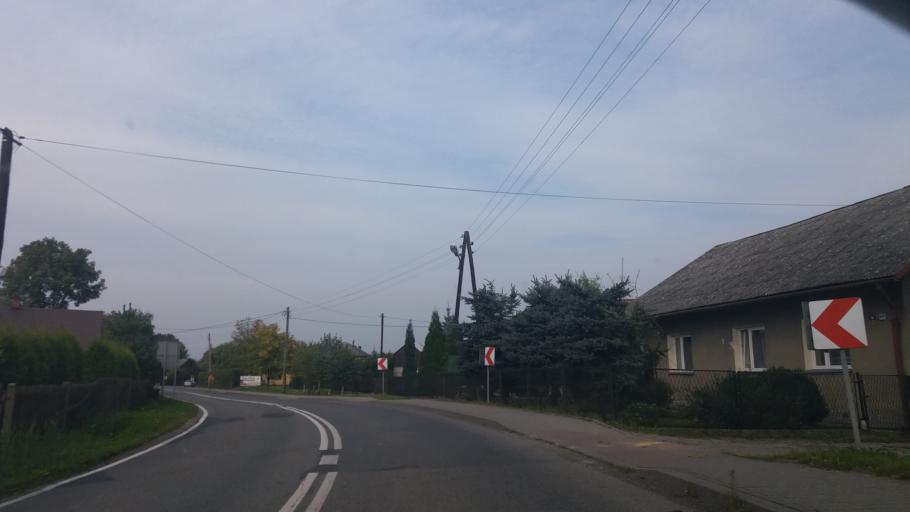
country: PL
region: Lesser Poland Voivodeship
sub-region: Powiat oswiecimski
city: Zator
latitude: 50.0137
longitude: 19.4350
